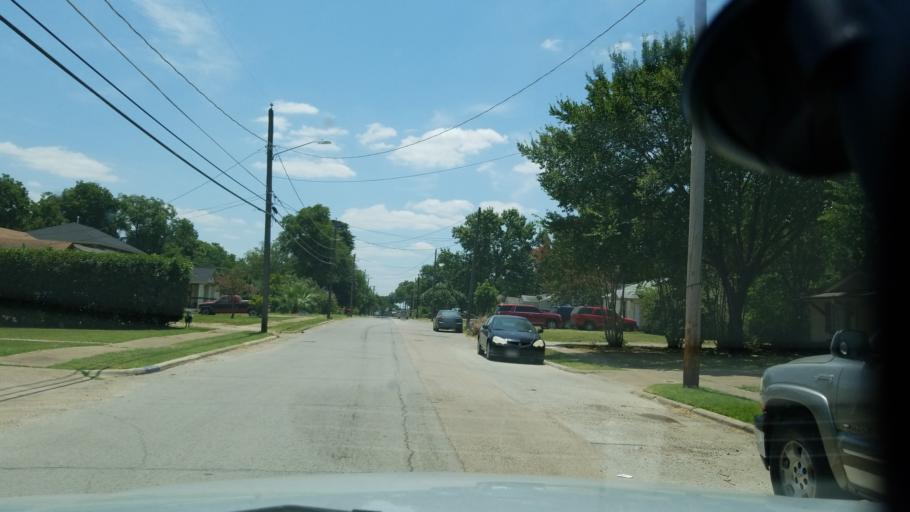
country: US
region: Texas
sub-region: Dallas County
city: Grand Prairie
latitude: 32.7527
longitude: -96.9617
